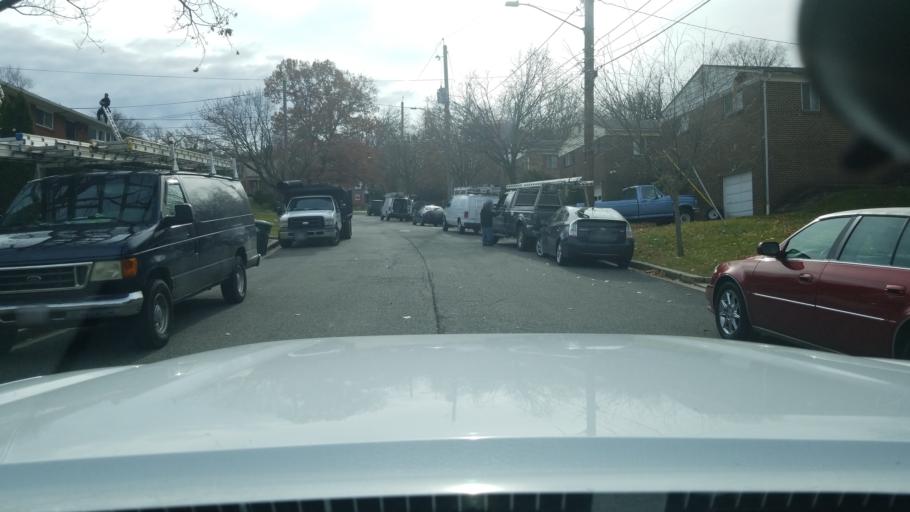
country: US
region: Maryland
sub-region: Prince George's County
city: Silver Hill
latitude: 38.8716
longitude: -76.9571
